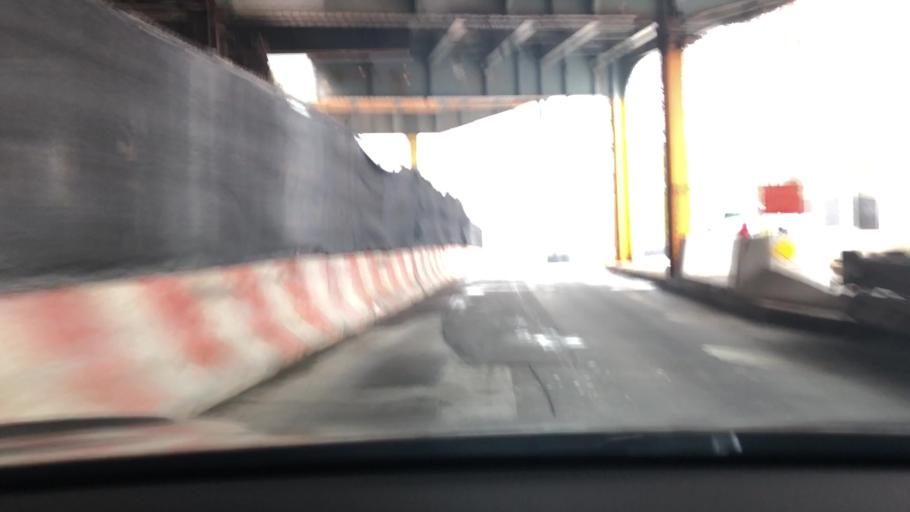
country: US
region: New York
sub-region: New York County
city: Inwood
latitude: 40.8762
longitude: -73.9247
